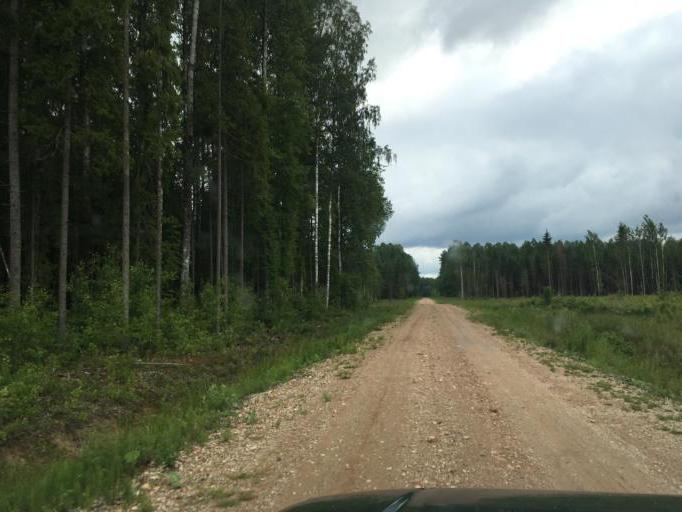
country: LV
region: Vilaka
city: Vilaka
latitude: 57.3873
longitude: 27.5074
